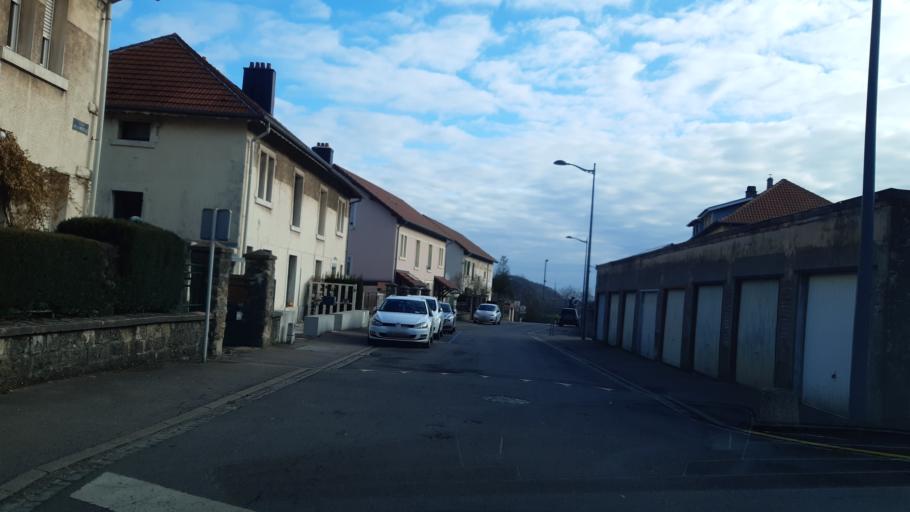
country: FR
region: Lorraine
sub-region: Departement de Meurthe-et-Moselle
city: Villerupt
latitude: 49.4721
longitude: 5.9347
